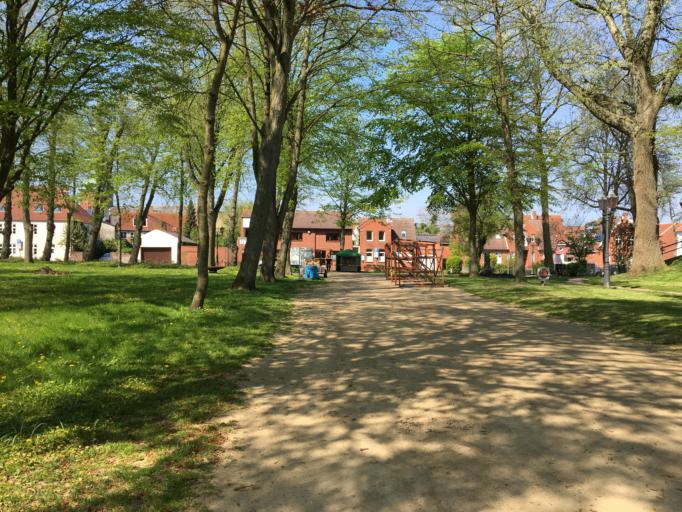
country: DE
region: Schleswig-Holstein
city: Tonning
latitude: 54.3154
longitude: 8.9425
